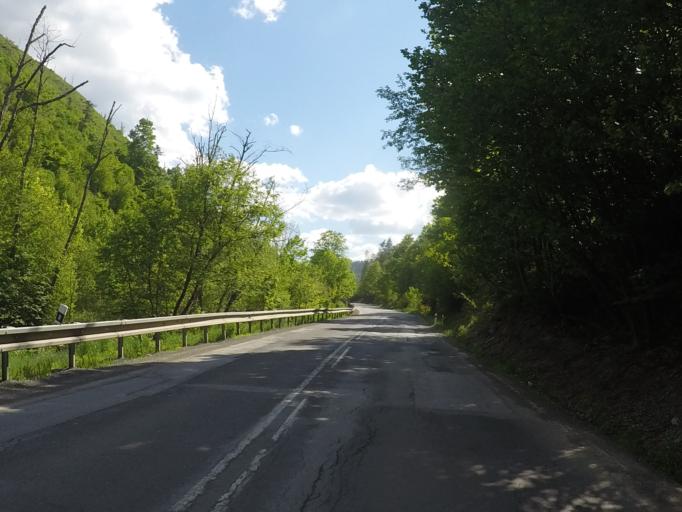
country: SK
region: Presovsky
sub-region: Okres Poprad
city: Poprad
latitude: 48.9501
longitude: 20.2939
